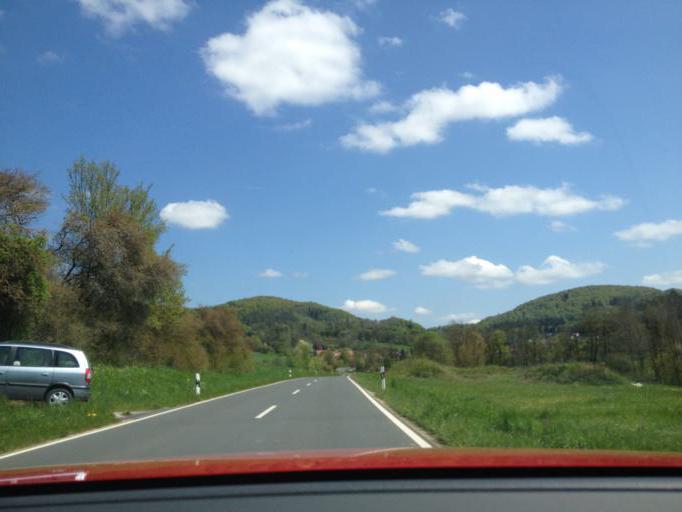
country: DE
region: Bavaria
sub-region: Regierungsbezirk Mittelfranken
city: Simmelsdorf
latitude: 49.5826
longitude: 11.3546
